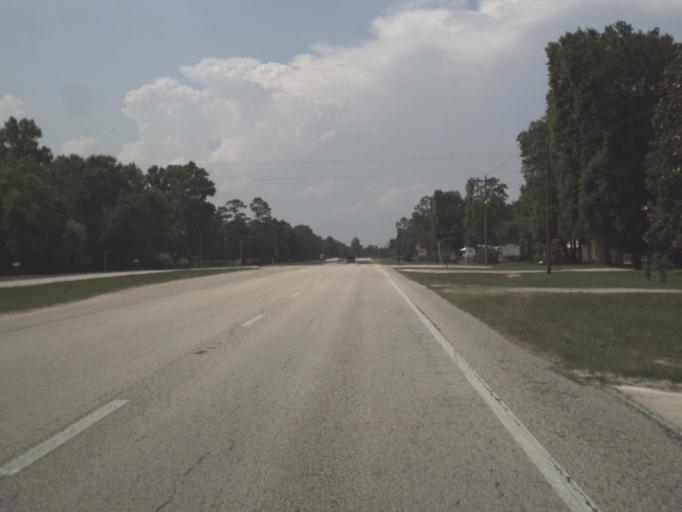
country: US
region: Florida
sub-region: Clay County
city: Green Cove Springs
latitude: 29.9252
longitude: -81.6847
